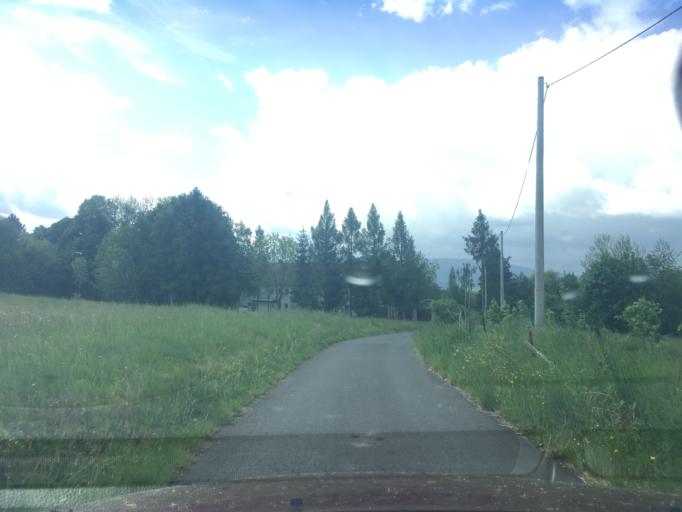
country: PL
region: Lower Silesian Voivodeship
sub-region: Powiat lubanski
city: Lesna
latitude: 50.9796
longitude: 15.3008
